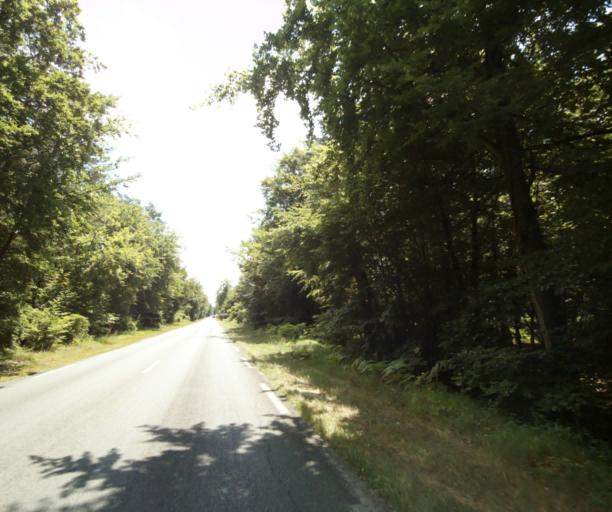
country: FR
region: Ile-de-France
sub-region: Departement de Seine-et-Marne
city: Bois-le-Roi
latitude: 48.4471
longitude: 2.7143
